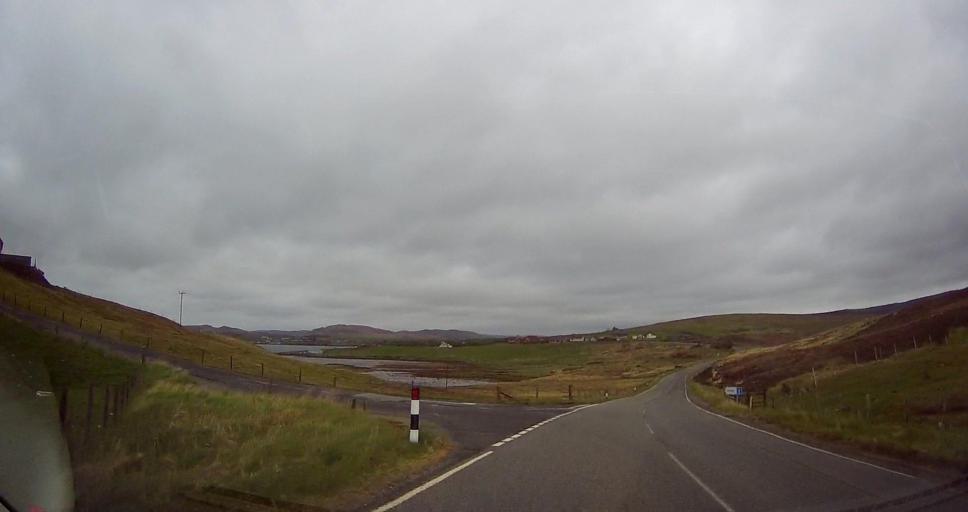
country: GB
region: Scotland
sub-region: Shetland Islands
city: Lerwick
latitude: 60.3798
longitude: -1.3423
